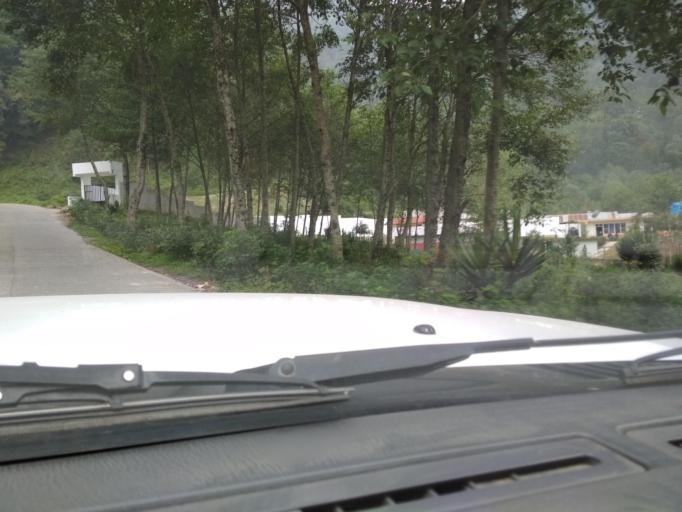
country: MX
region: Veracruz
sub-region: La Perla
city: Metlac Hernandez (Metlac Primero)
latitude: 18.9756
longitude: -97.1450
